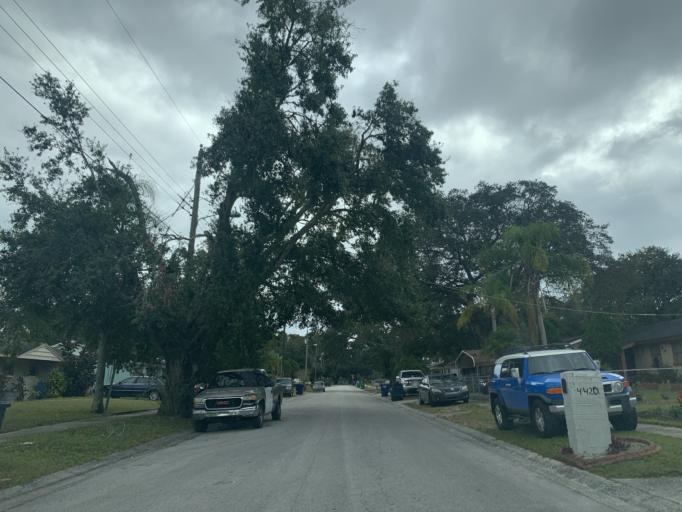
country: US
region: Florida
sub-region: Hillsborough County
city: East Lake-Orient Park
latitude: 27.9870
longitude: -82.4038
